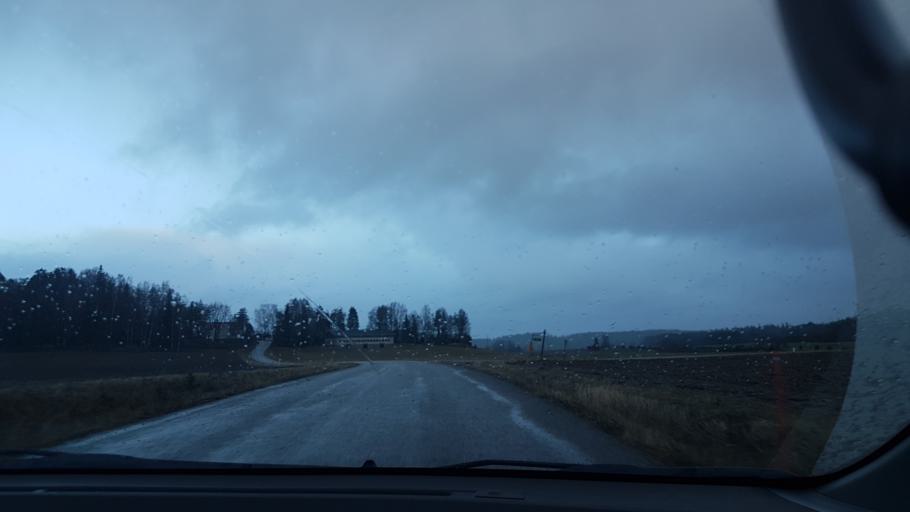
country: FI
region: Uusimaa
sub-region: Helsinki
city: Lohja
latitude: 60.2088
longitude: 24.1007
